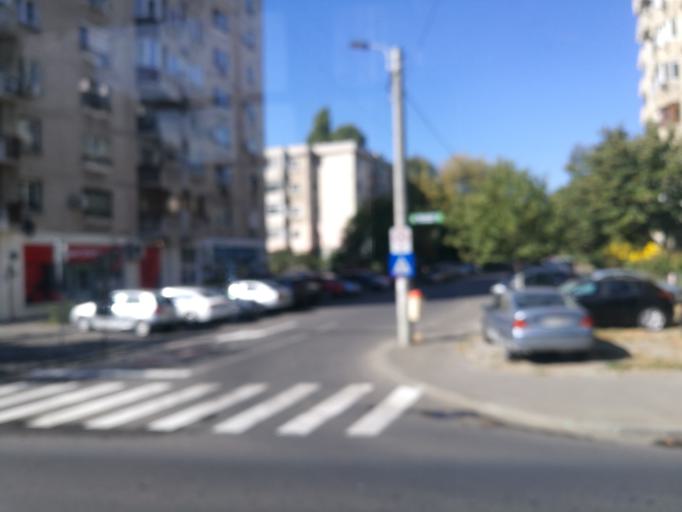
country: RO
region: Ilfov
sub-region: Comuna Chiajna
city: Rosu
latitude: 44.4393
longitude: 26.0349
